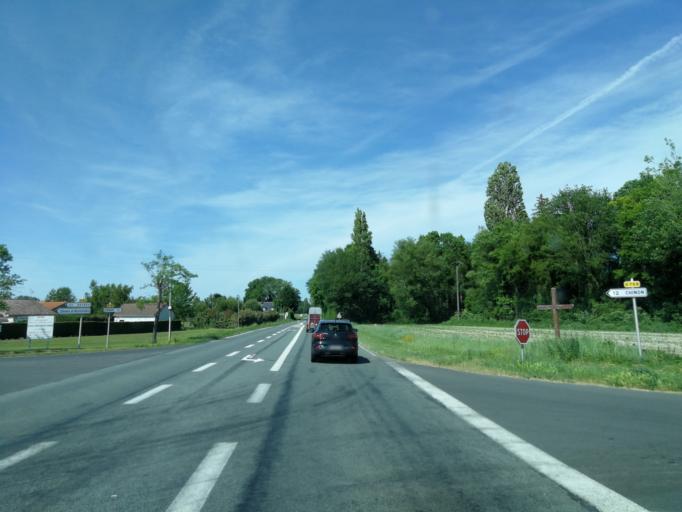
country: FR
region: Centre
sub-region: Departement d'Indre-et-Loire
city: Ligre
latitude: 47.0895
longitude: 0.1824
